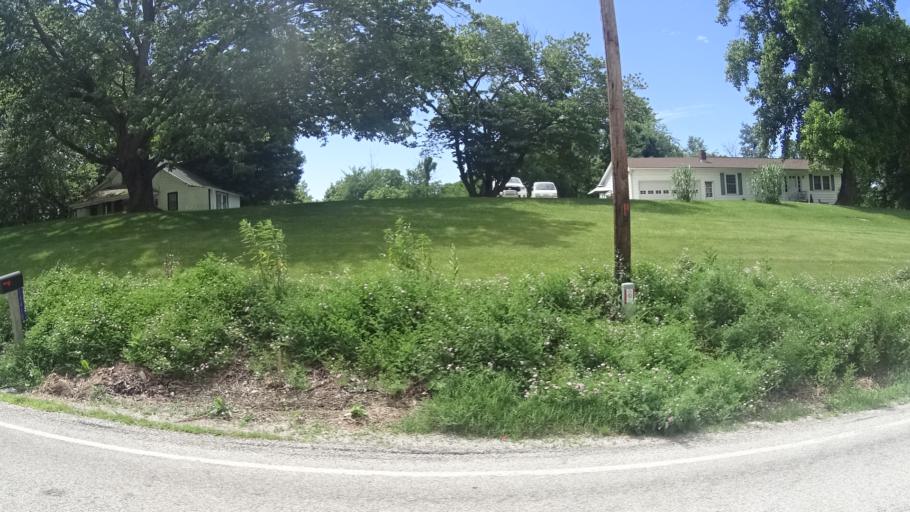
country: US
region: Ohio
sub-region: Erie County
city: Milan
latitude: 41.2902
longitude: -82.6148
